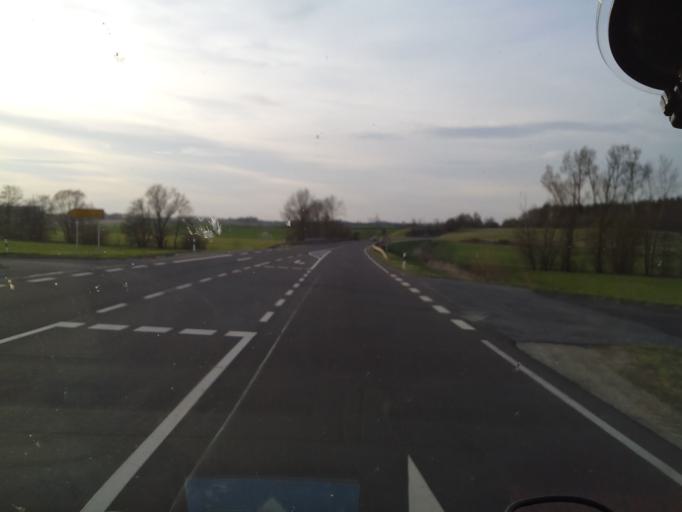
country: DE
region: Bavaria
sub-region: Regierungsbezirk Unterfranken
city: Pfarrweisach
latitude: 50.1169
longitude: 10.7668
